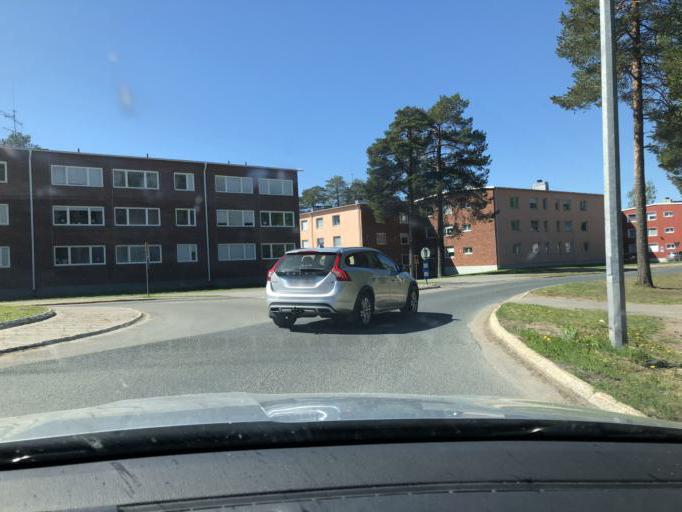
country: SE
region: Norrbotten
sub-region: Kalix Kommun
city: Kalix
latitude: 65.8527
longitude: 23.1588
